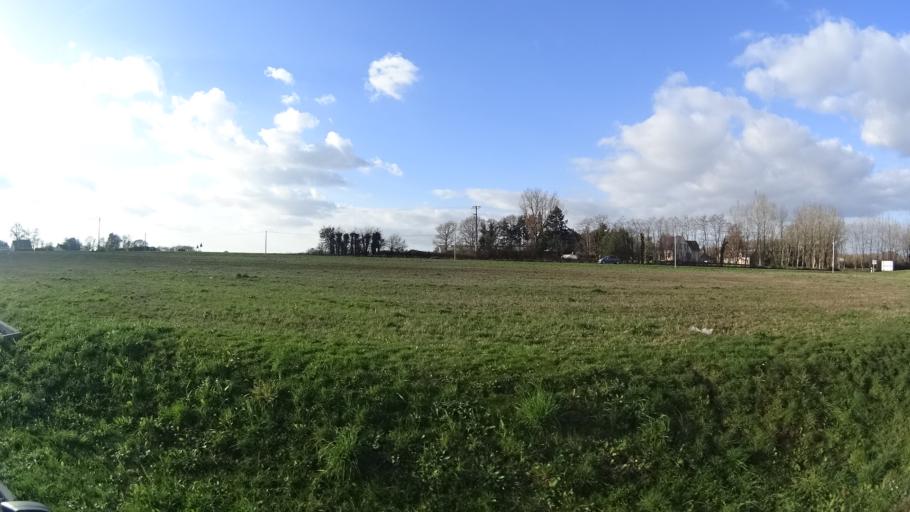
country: FR
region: Pays de la Loire
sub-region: Departement de la Loire-Atlantique
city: Guemene-Penfao
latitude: 47.6364
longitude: -1.8045
